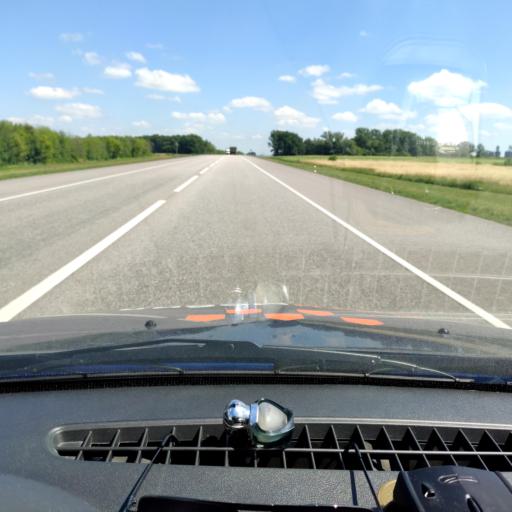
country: RU
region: Orjol
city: Orel
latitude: 52.8516
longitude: 36.2365
